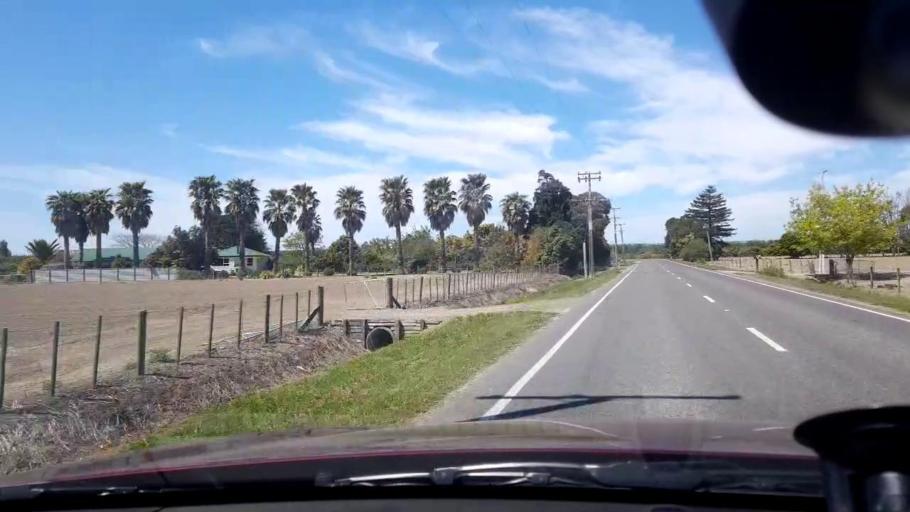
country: NZ
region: Gisborne
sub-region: Gisborne District
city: Gisborne
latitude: -38.6359
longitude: 177.9303
